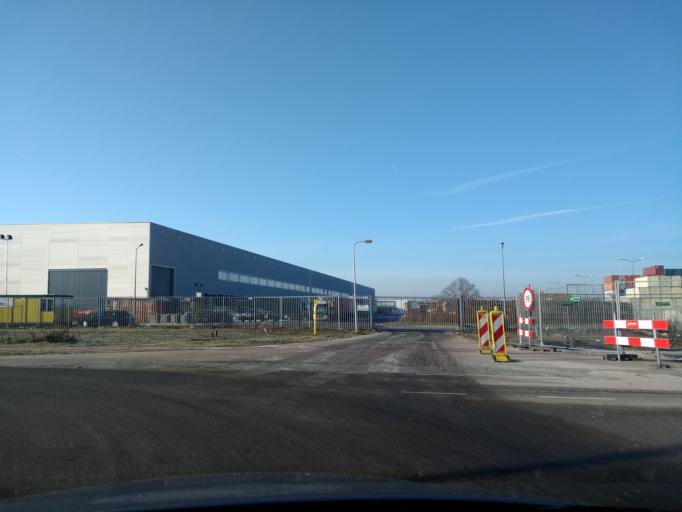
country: NL
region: Overijssel
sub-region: Gemeente Hengelo
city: Hengelo
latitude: 52.2456
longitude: 6.7887
